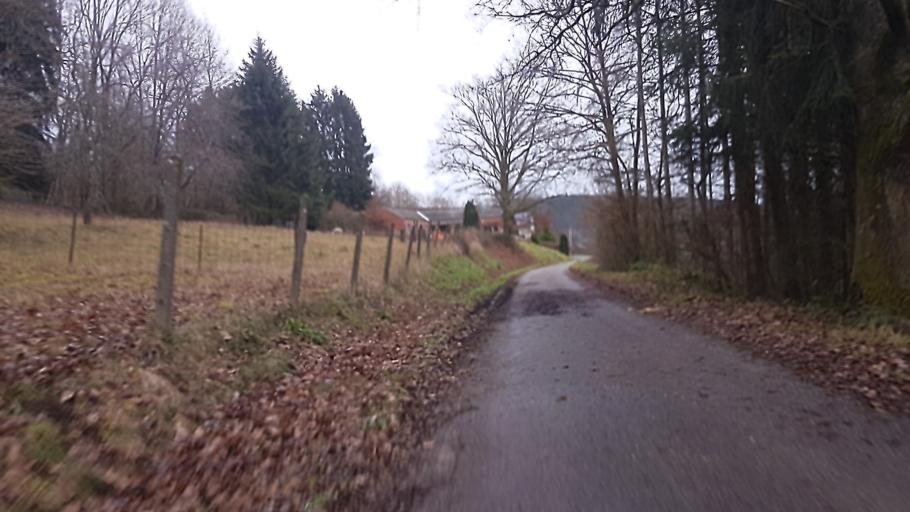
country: BE
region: Wallonia
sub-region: Province de Namur
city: Couvin
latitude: 50.0688
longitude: 4.6050
